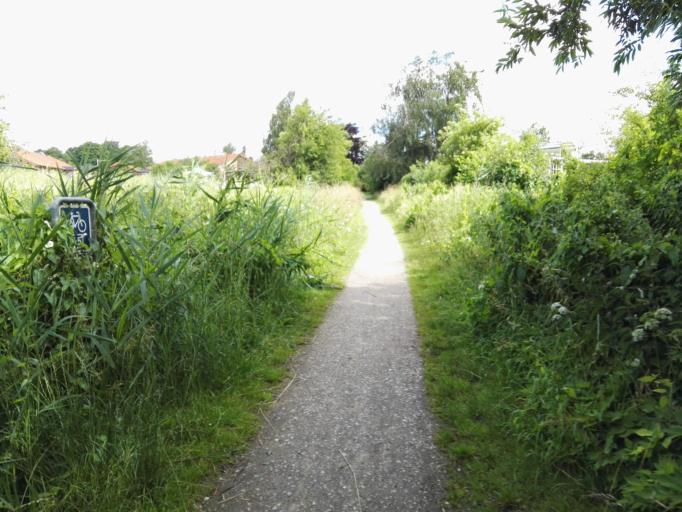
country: DK
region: Capital Region
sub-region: Herlev Kommune
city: Herlev
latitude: 55.7339
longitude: 12.4092
